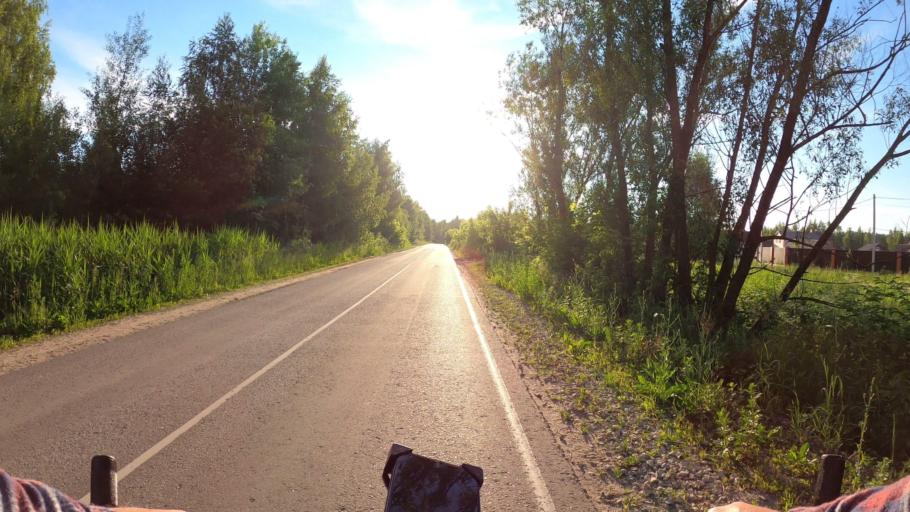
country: RU
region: Moskovskaya
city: Ashitkovo
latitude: 55.4270
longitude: 38.5711
